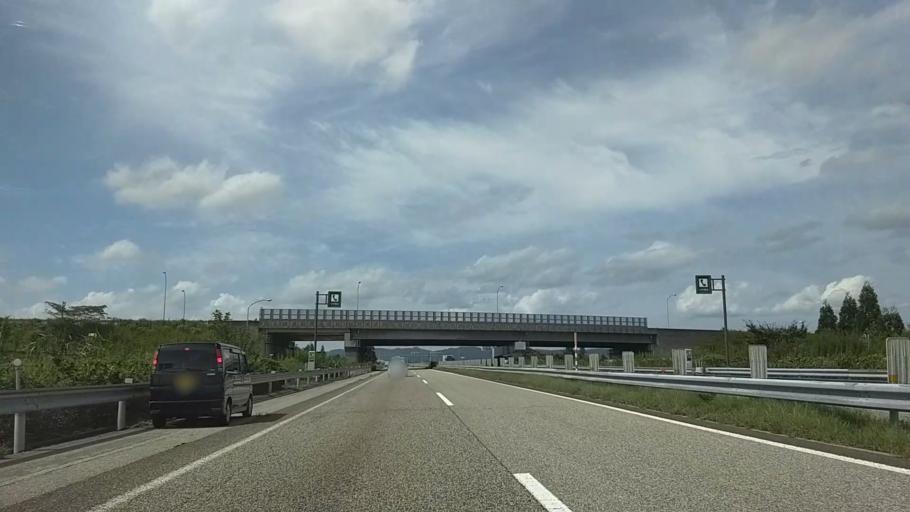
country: JP
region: Toyama
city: Nanto-shi
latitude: 36.6300
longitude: 136.9105
